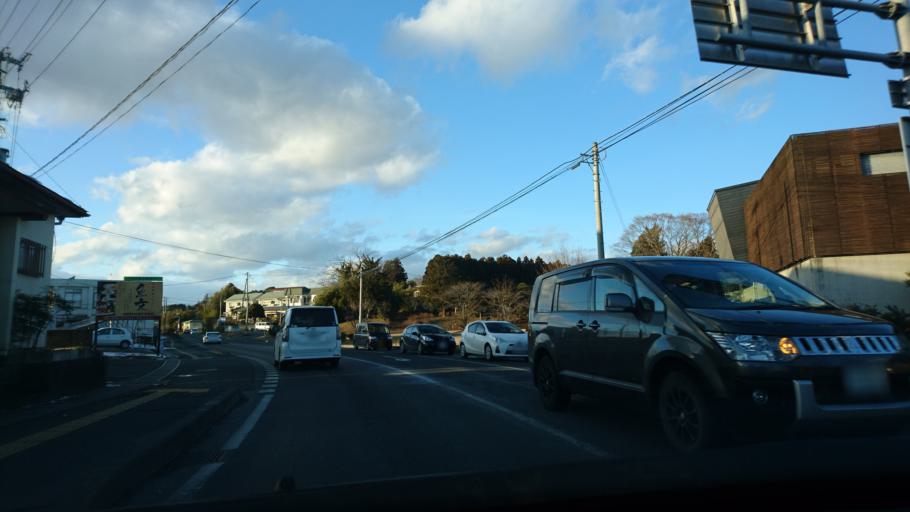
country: JP
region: Miyagi
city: Wakuya
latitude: 38.6936
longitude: 141.1947
